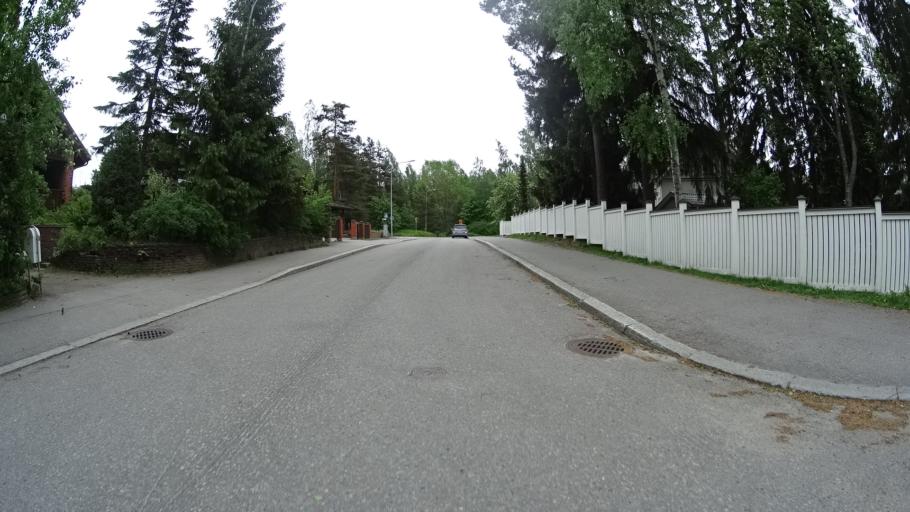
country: FI
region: Uusimaa
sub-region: Helsinki
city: Vantaa
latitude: 60.2660
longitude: 25.0650
